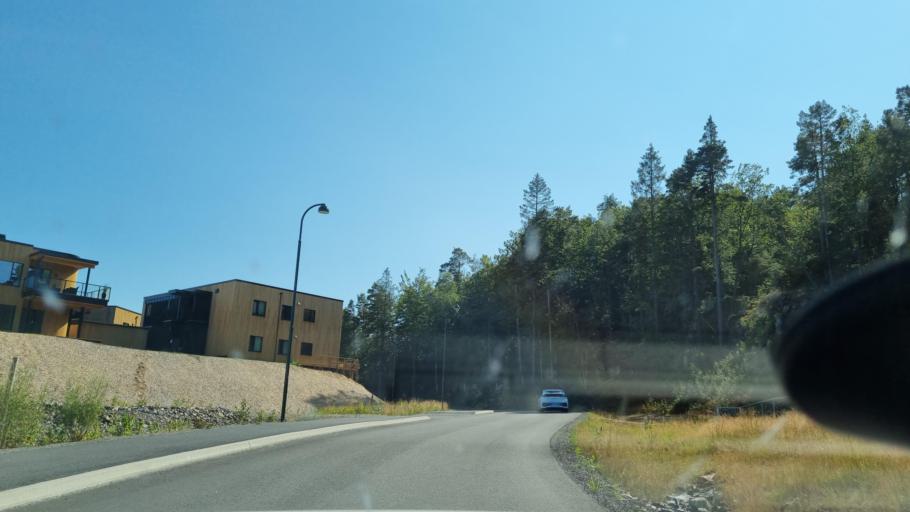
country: NO
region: Aust-Agder
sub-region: Arendal
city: Arendal
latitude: 58.4586
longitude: 8.8136
